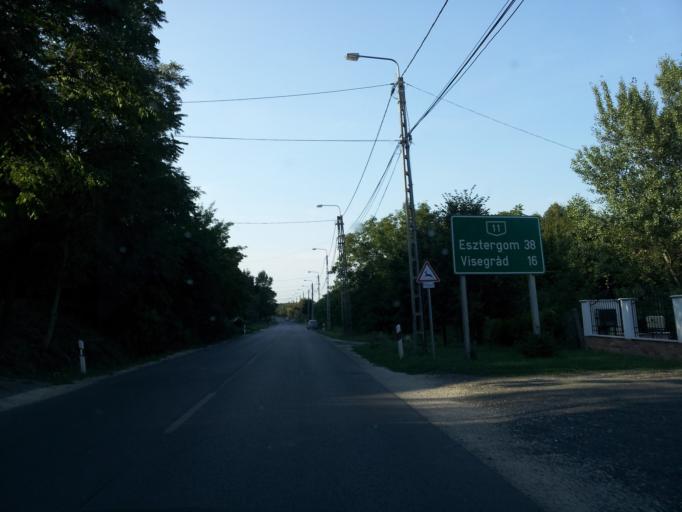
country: HU
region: Pest
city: Leanyfalu
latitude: 47.7324
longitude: 19.0885
